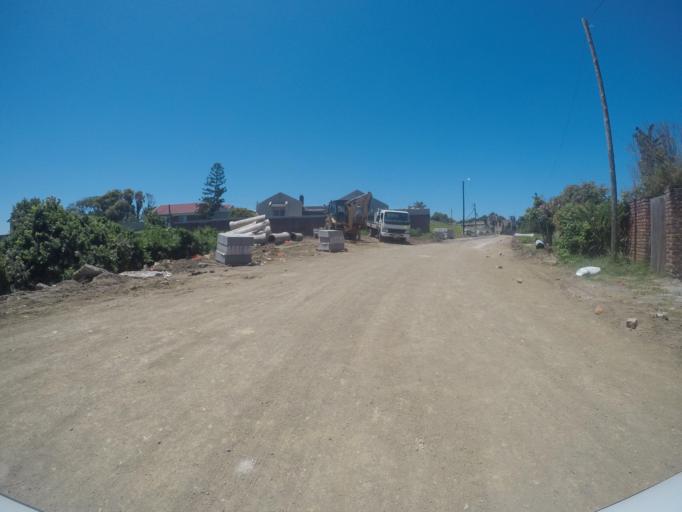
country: ZA
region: Eastern Cape
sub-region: Buffalo City Metropolitan Municipality
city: East London
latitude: -32.9561
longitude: 27.9951
